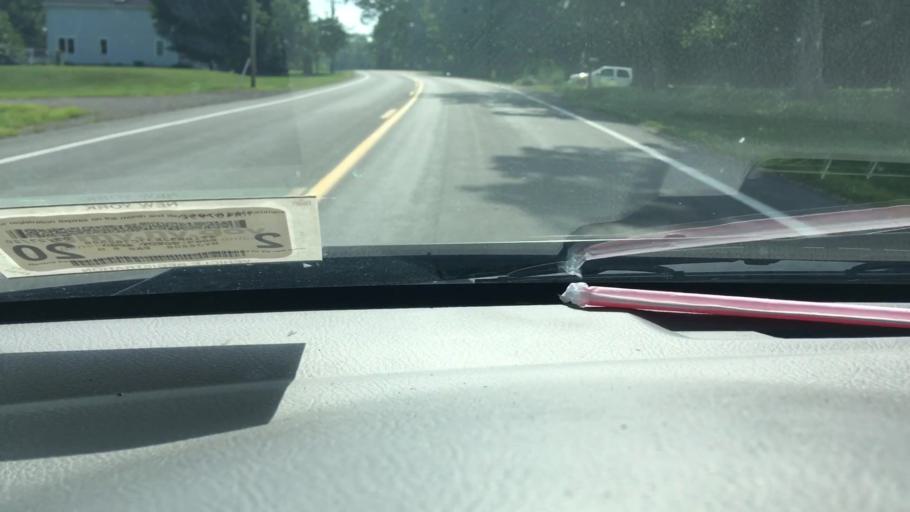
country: US
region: New York
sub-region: Genesee County
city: Batavia
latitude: 43.0495
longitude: -78.1320
